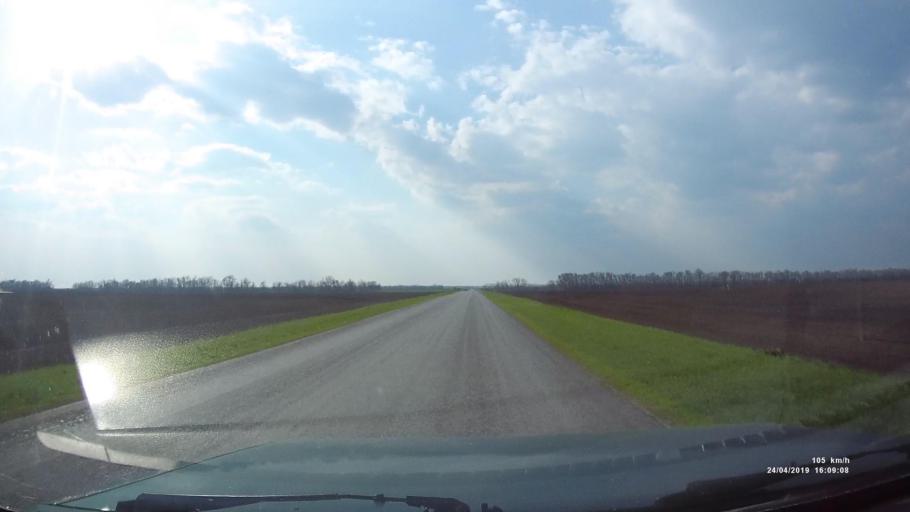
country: RU
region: Rostov
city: Sovetskoye
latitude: 46.7056
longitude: 42.2939
